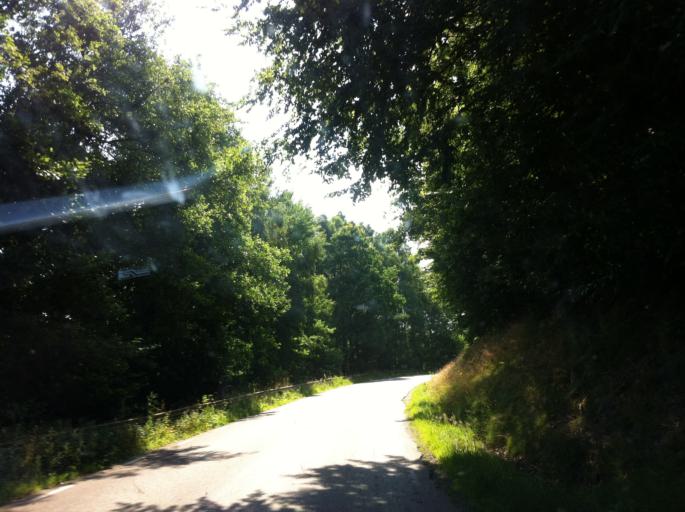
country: SE
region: Skane
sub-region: Hoors Kommun
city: Hoeoer
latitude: 56.0030
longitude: 13.4888
